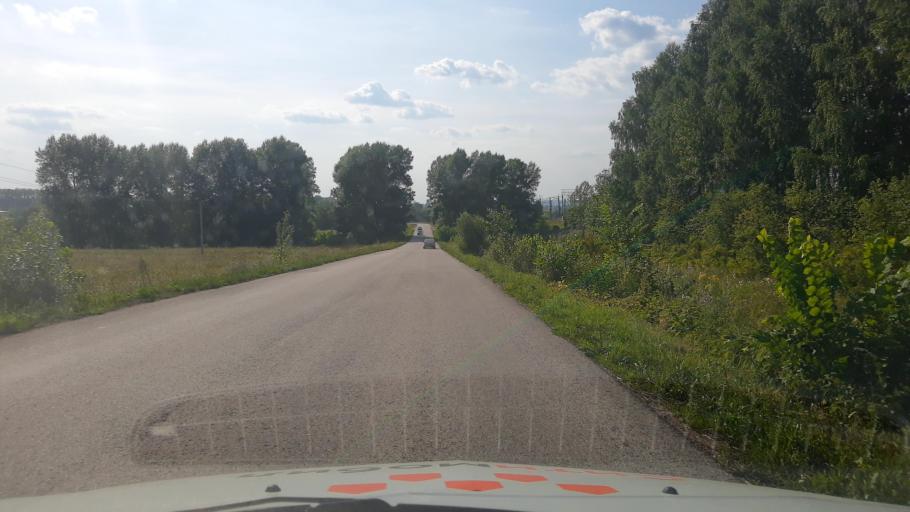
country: RU
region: Bashkortostan
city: Kabakovo
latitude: 54.6620
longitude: 56.1842
